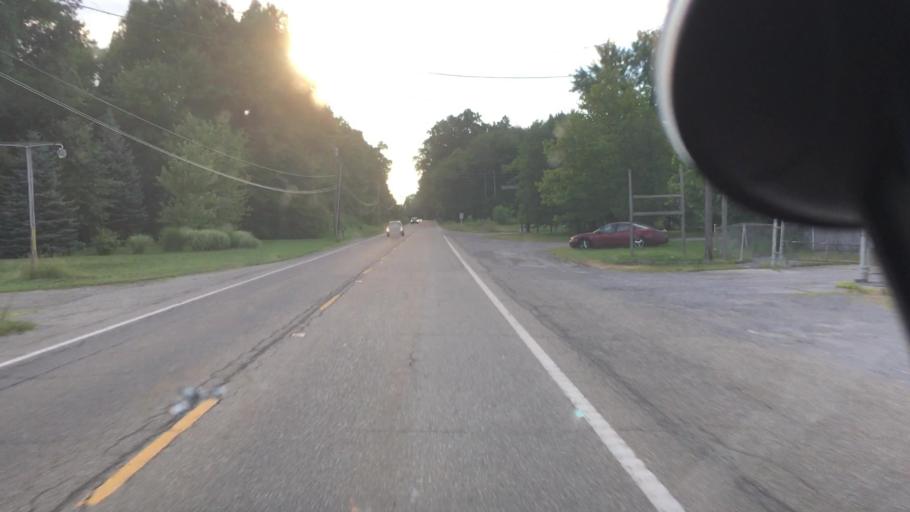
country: US
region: Ohio
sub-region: Columbiana County
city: New Waterford
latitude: 40.8768
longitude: -80.5934
